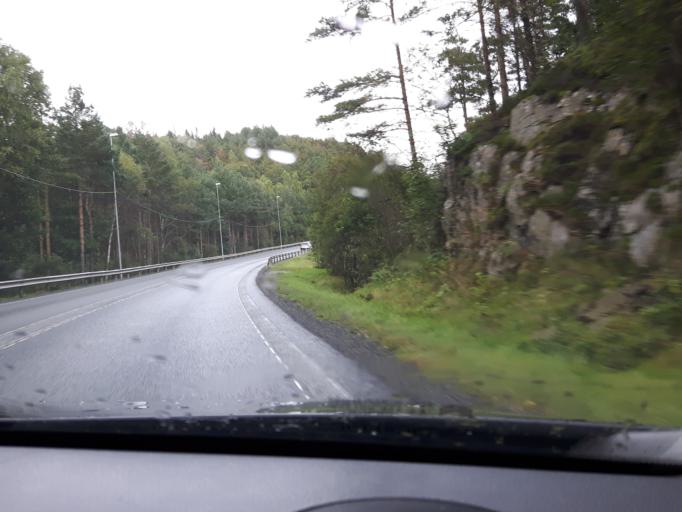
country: NO
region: Vest-Agder
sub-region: Marnardal
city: Helland
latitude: 58.0952
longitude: 7.6311
